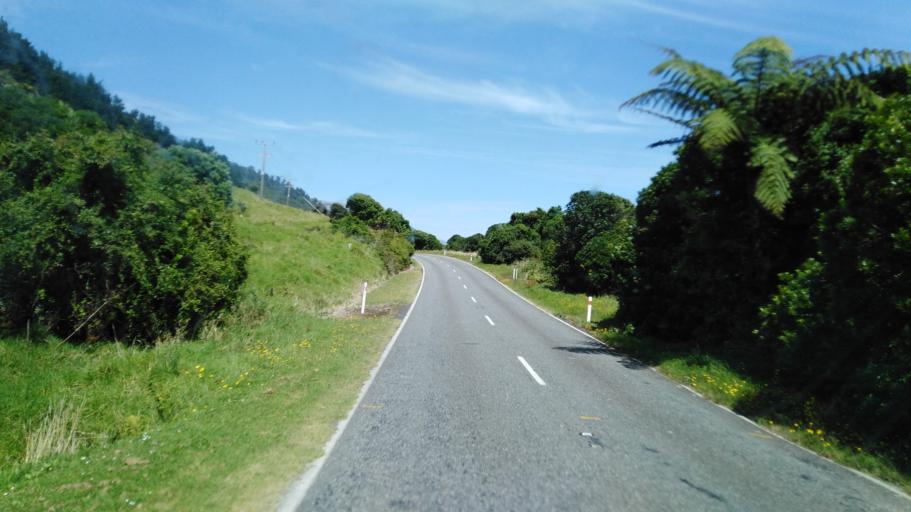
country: NZ
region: West Coast
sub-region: Buller District
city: Westport
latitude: -41.5761
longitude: 171.9011
